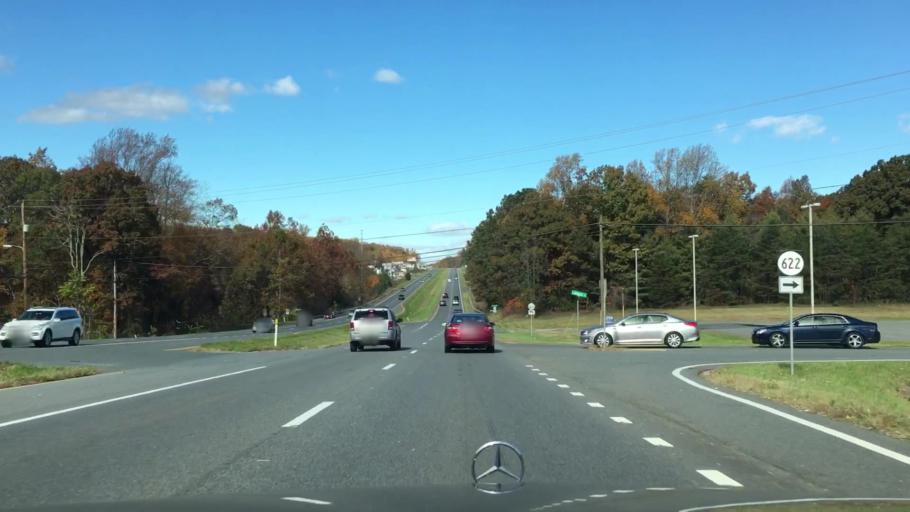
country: US
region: Virginia
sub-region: Campbell County
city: Rustburg
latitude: 37.2882
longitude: -79.1675
